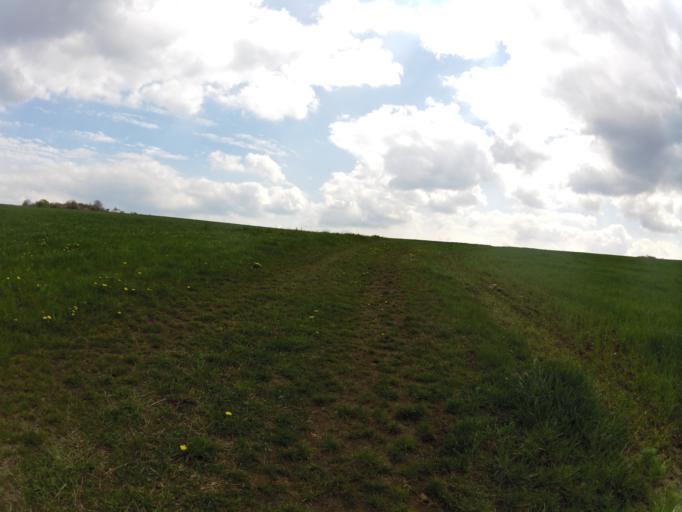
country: DE
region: Bavaria
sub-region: Regierungsbezirk Unterfranken
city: Hettstadt
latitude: 49.7941
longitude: 9.7927
